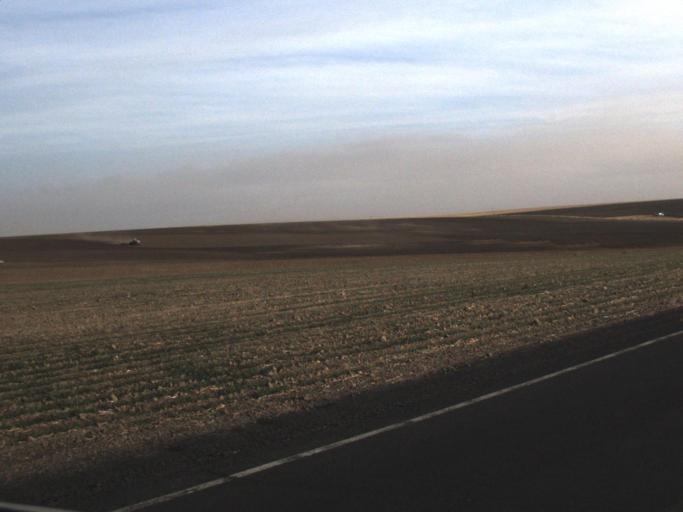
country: US
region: Washington
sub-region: Adams County
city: Ritzville
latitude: 47.2956
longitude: -118.6902
